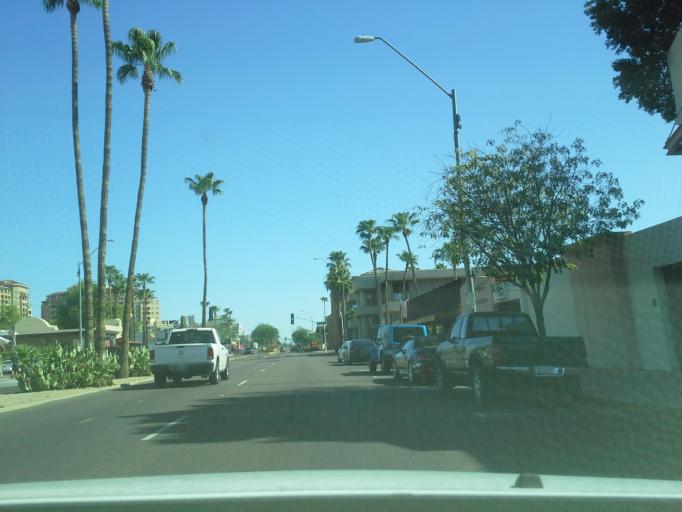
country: US
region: Arizona
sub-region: Maricopa County
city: Scottsdale
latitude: 33.4972
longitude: -111.9260
